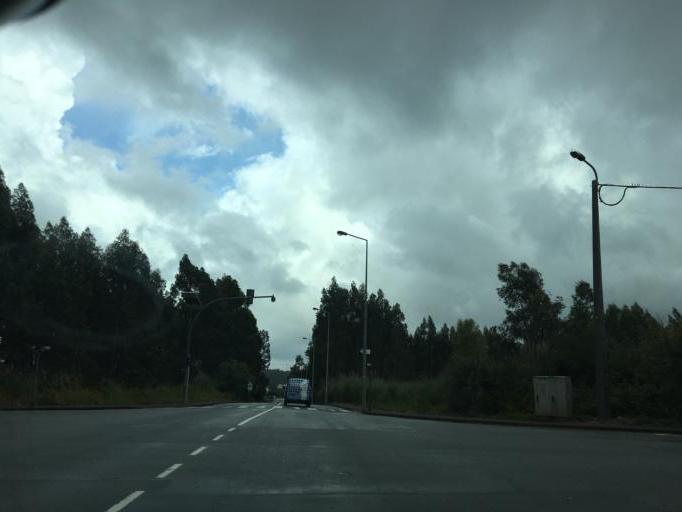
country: PT
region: Porto
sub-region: Maia
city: Nogueira
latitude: 41.2565
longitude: -8.5964
